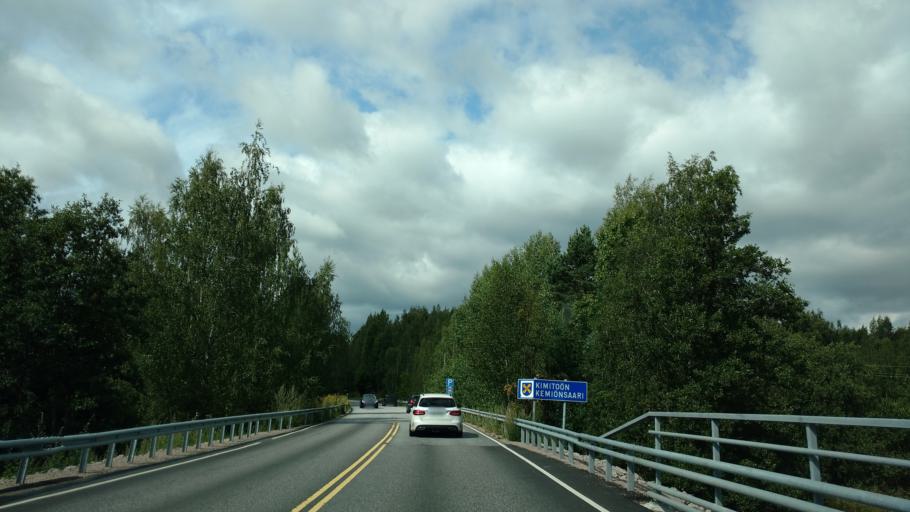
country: FI
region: Varsinais-Suomi
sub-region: Salo
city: Saerkisalo
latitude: 60.1890
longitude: 22.8766
